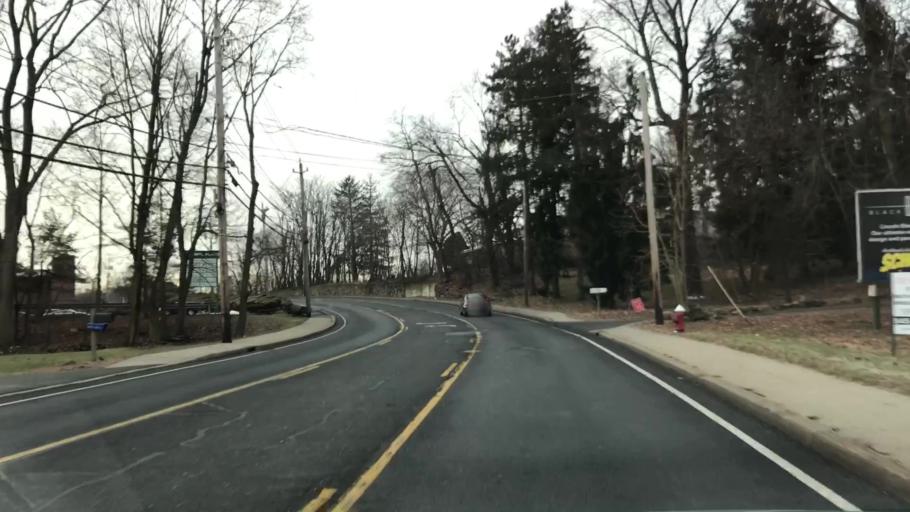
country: US
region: New York
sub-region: Rockland County
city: Stony Point
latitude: 41.2211
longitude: -73.9859
